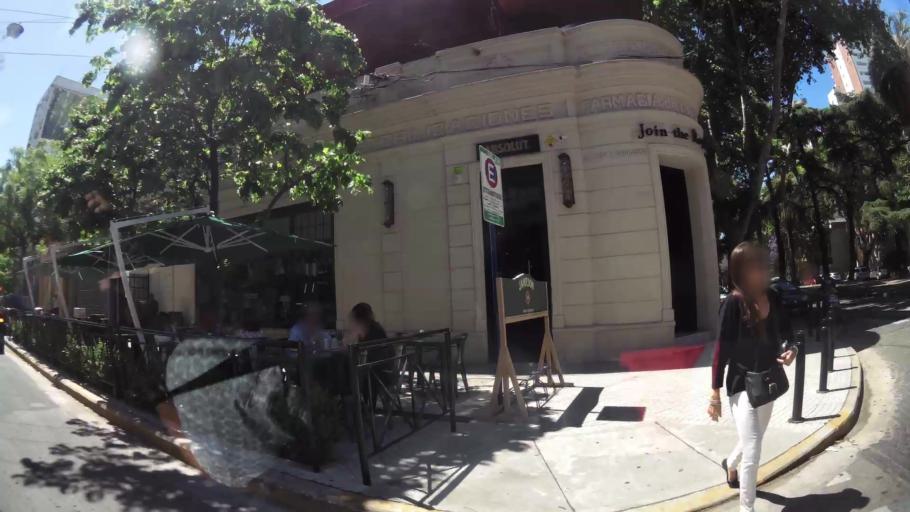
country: AR
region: Santa Fe
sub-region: Departamento de Rosario
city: Rosario
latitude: -32.9332
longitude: -60.6508
